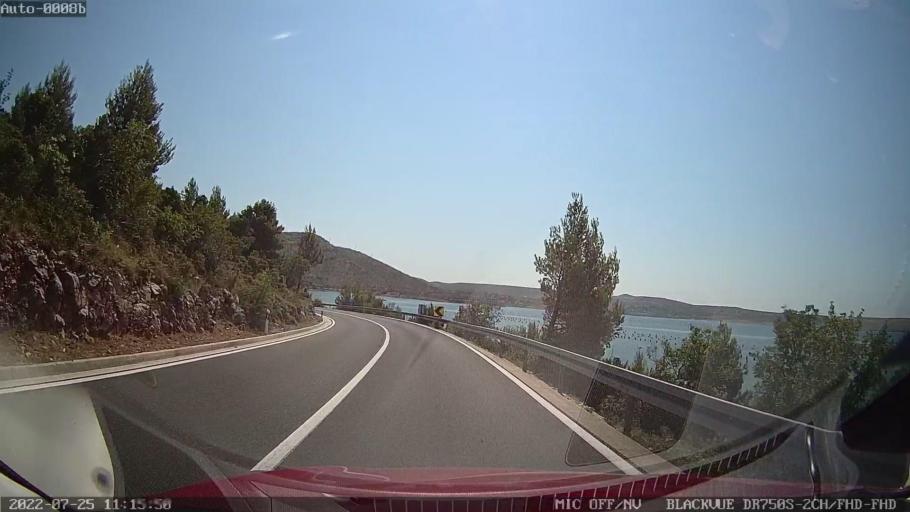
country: HR
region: Zadarska
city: Posedarje
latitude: 44.2710
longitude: 15.5150
